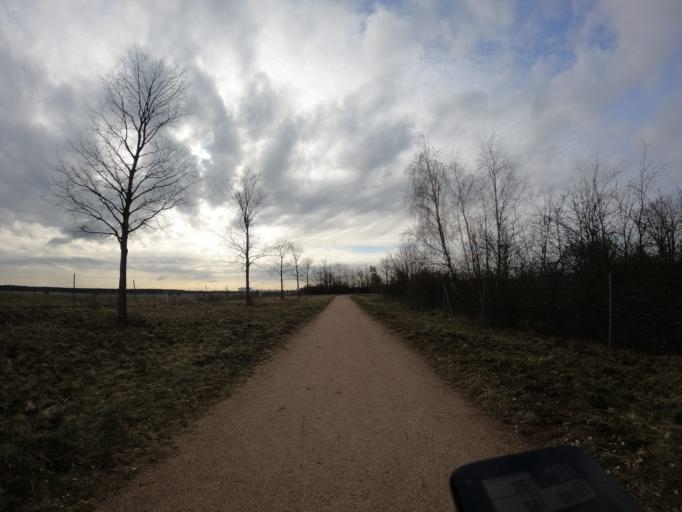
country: DE
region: Brandenburg
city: Schonefeld
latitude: 52.3883
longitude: 13.5359
